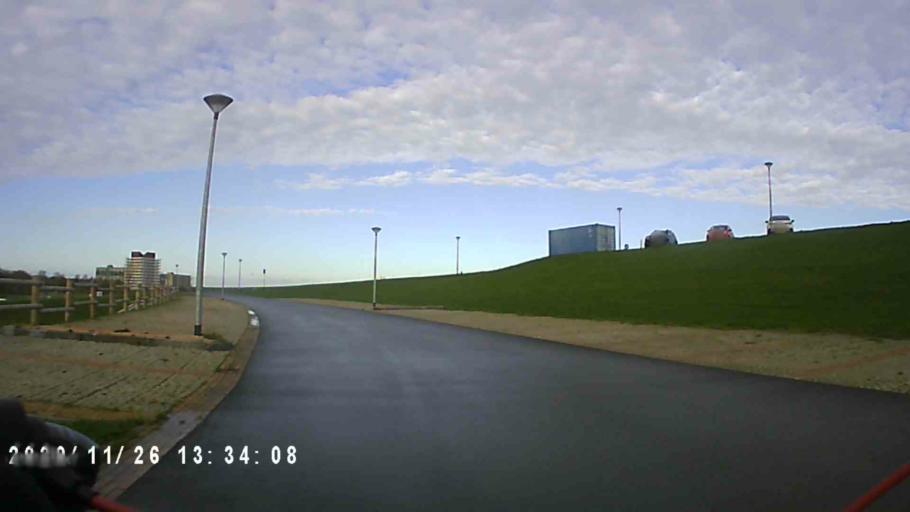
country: NL
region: Groningen
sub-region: Gemeente Delfzijl
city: Delfzijl
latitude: 53.3358
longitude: 6.9272
